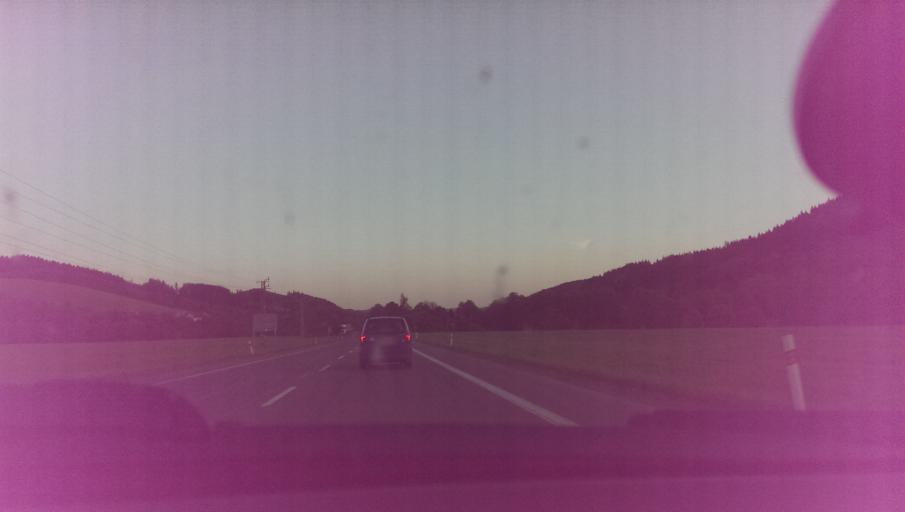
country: CZ
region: Zlin
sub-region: Okres Vsetin
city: Vsetin
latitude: 49.3149
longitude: 18.0049
